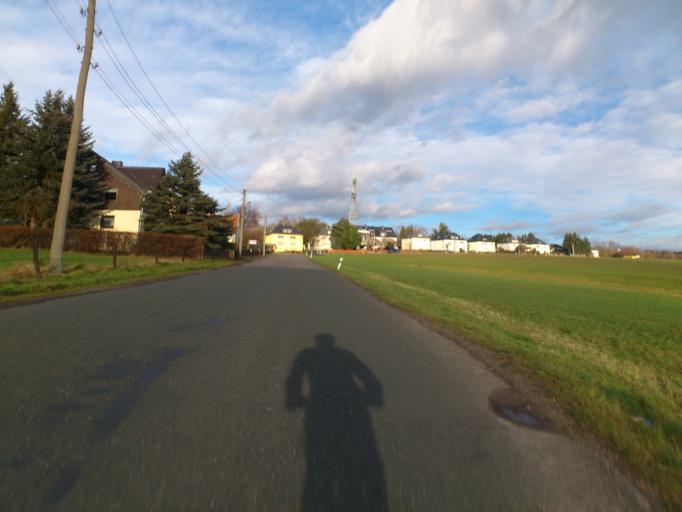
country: DE
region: Saxony
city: Neukirchen
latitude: 50.7792
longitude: 12.8783
